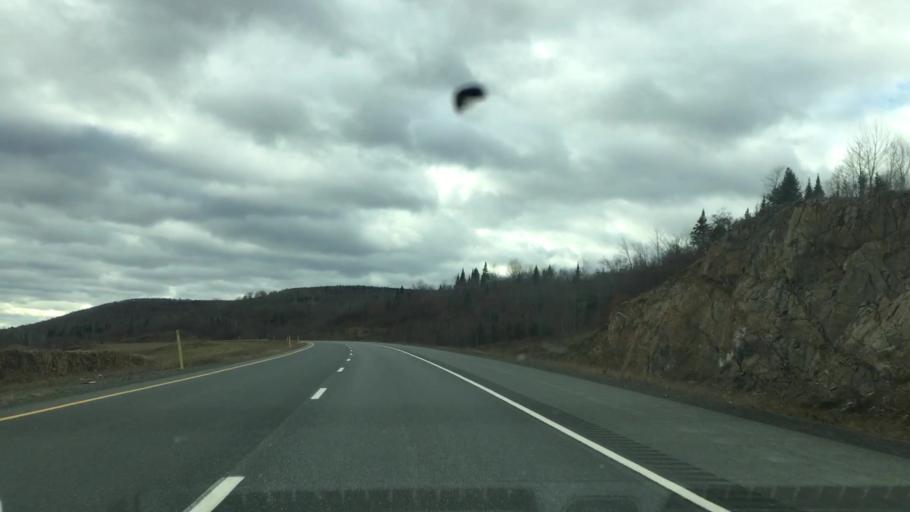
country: US
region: Maine
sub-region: Aroostook County
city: Fort Fairfield
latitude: 46.7009
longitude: -67.7402
